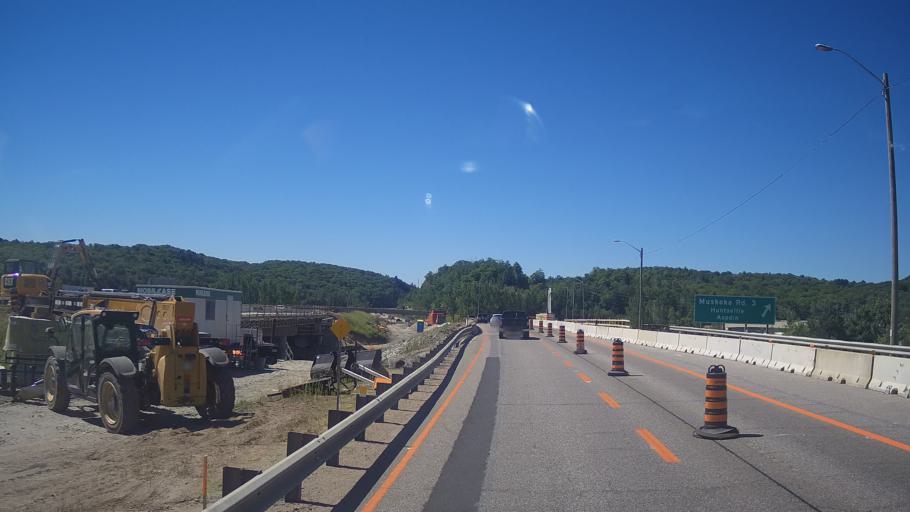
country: CA
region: Ontario
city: Huntsville
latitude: 45.3168
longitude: -79.2447
